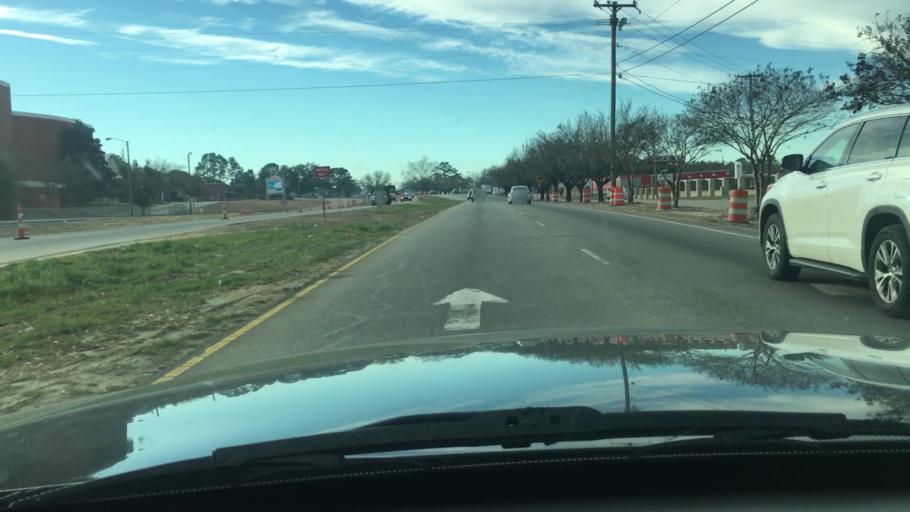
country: US
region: North Carolina
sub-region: Cumberland County
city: Fayetteville
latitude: 35.0182
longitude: -78.8963
